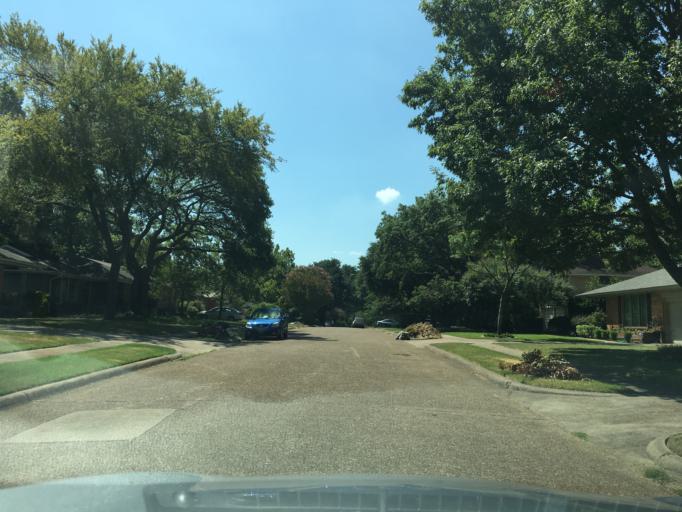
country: US
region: Texas
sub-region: Dallas County
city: Garland
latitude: 32.8546
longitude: -96.6905
